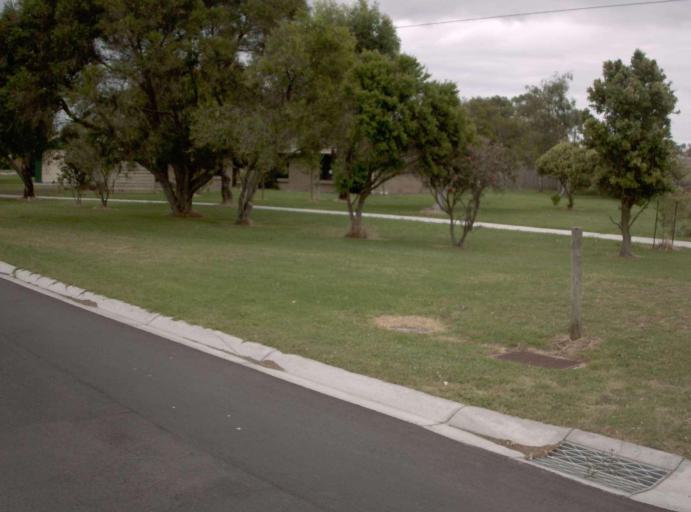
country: AU
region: Victoria
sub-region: Bass Coast
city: North Wonthaggi
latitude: -38.5949
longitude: 145.6070
